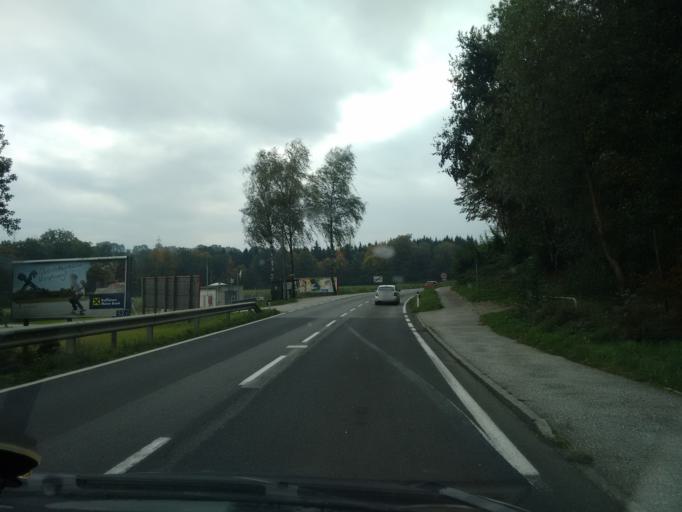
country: AT
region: Upper Austria
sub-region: Politischer Bezirk Steyr-Land
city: Bad Hall
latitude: 48.0533
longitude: 14.2023
